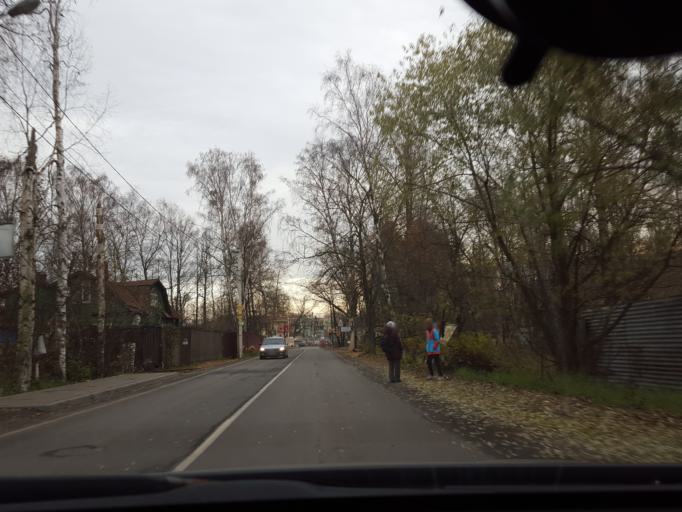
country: RU
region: St.-Petersburg
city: Shuvalovo
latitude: 60.0434
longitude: 30.2980
